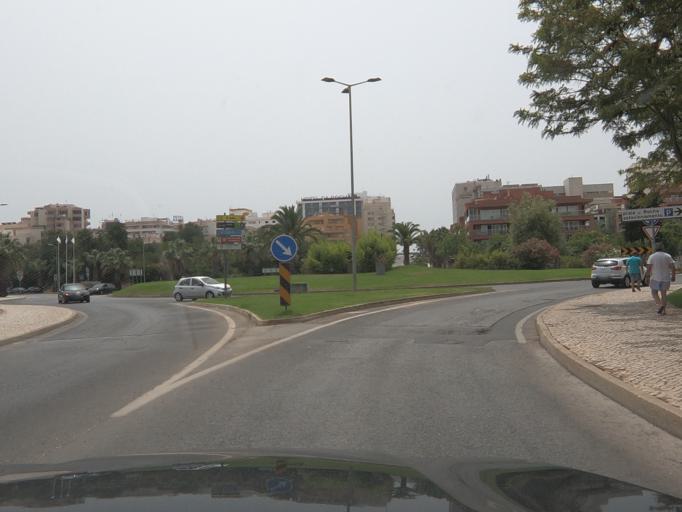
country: PT
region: Faro
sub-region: Portimao
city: Portimao
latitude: 37.1224
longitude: -8.5352
